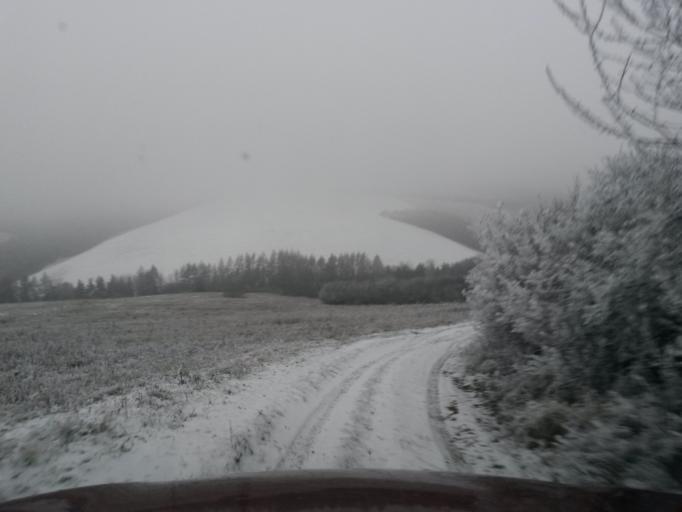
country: SK
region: Presovsky
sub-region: Okres Presov
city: Presov
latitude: 48.9766
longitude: 21.1203
